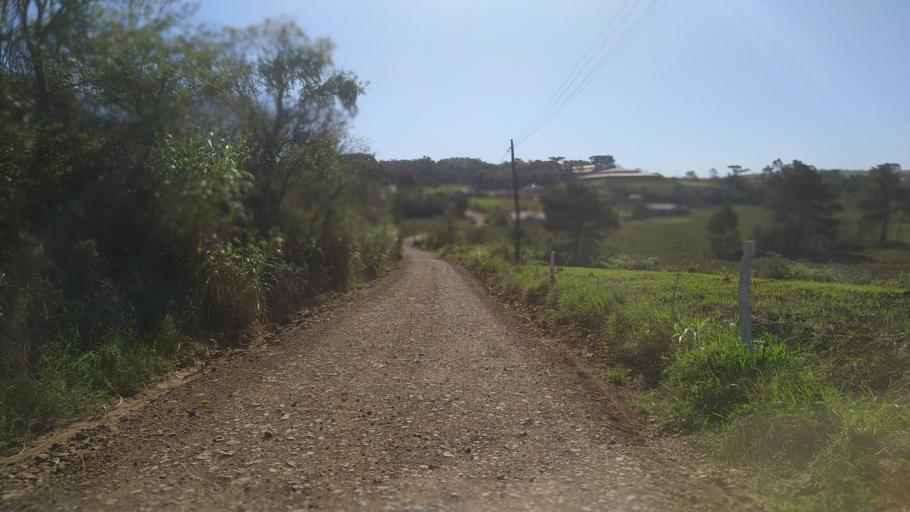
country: BR
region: Santa Catarina
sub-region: Chapeco
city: Chapeco
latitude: -27.1490
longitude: -52.5954
